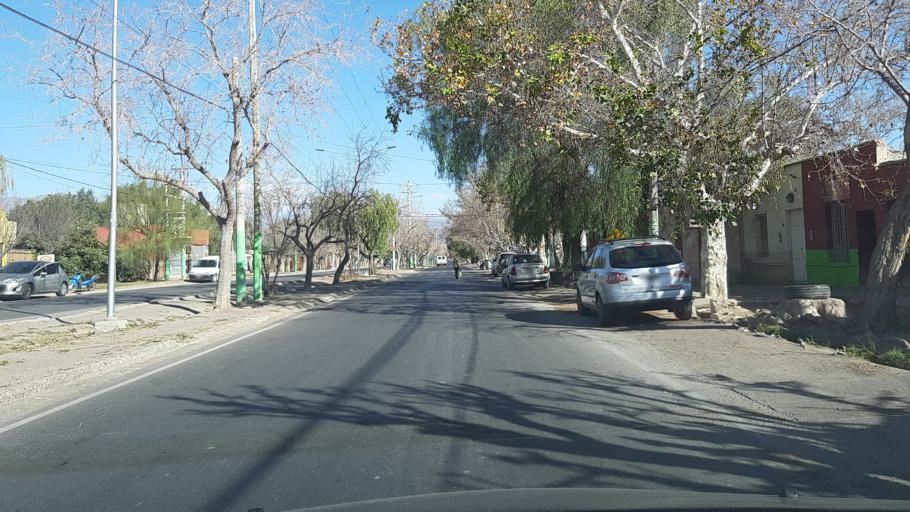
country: AR
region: San Juan
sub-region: Departamento de Rivadavia
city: Rivadavia
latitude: -31.5269
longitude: -68.6338
